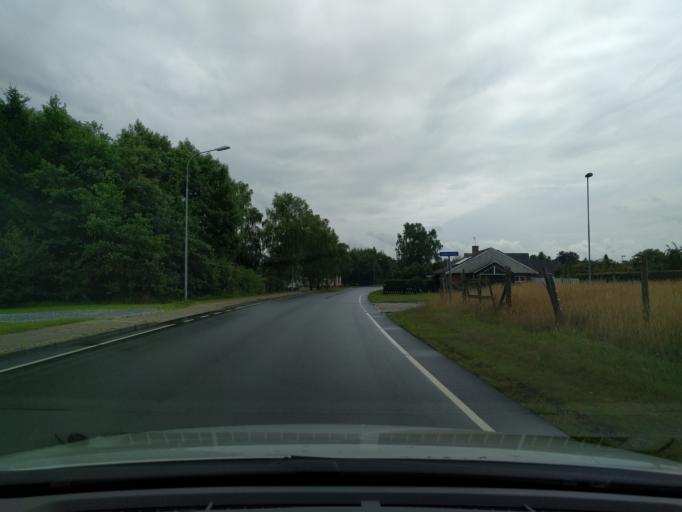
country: DK
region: Central Jutland
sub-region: Skanderborg Kommune
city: Ry
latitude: 56.0882
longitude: 9.7782
